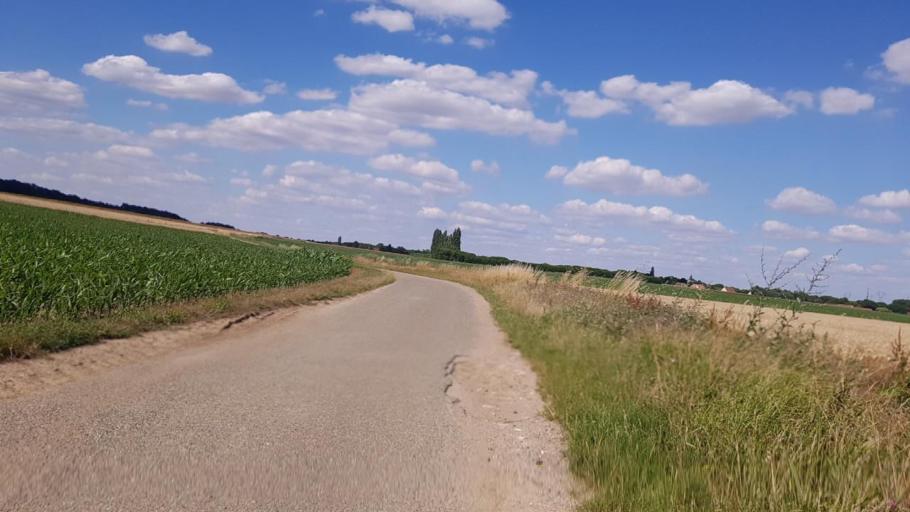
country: FR
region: Picardie
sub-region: Departement de l'Oise
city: Ver-sur-Launette
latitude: 49.0980
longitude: 2.6762
